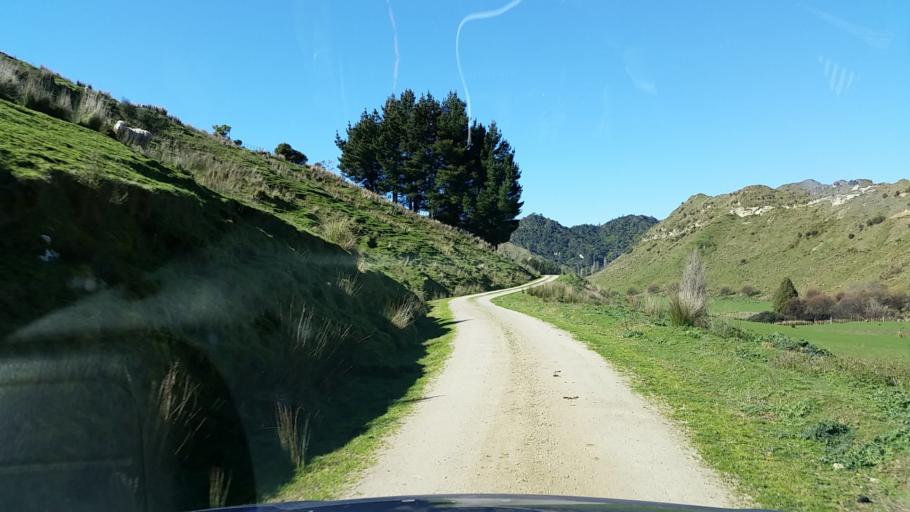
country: NZ
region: Manawatu-Wanganui
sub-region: Wanganui District
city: Wanganui
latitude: -39.6768
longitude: 174.8581
